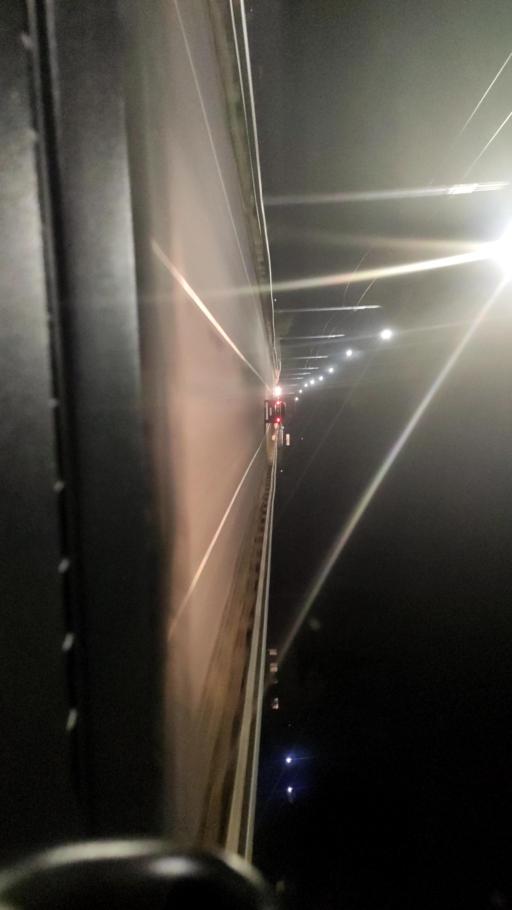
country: RU
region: Voronezj
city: Novaya Usman'
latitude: 51.6240
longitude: 39.3982
